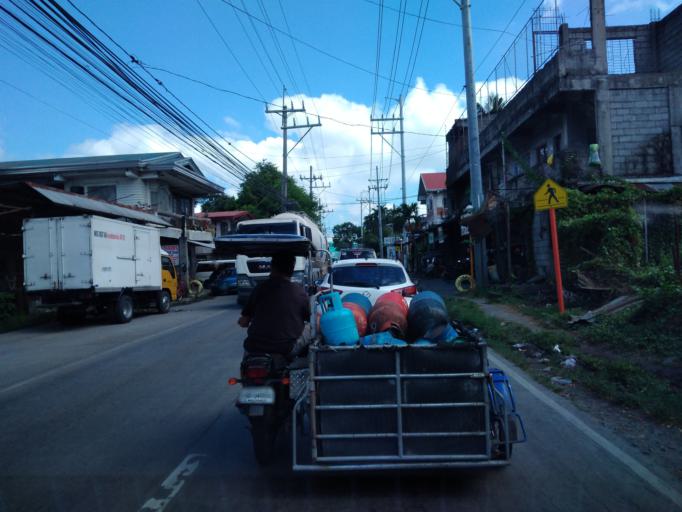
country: PH
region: Central Luzon
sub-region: Province of Bulacan
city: Guyong
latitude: 14.8392
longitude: 120.9789
